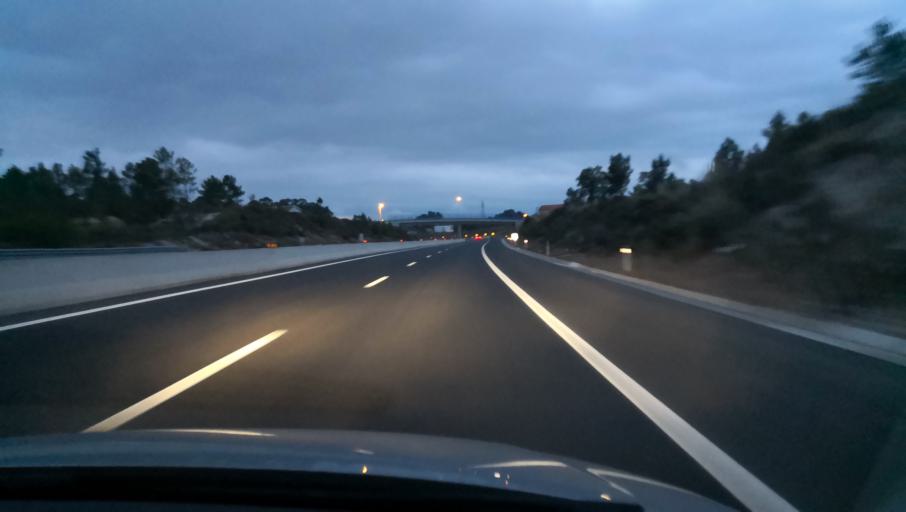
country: PT
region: Setubal
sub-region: Seixal
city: Arrentela
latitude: 38.5966
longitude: -9.1013
